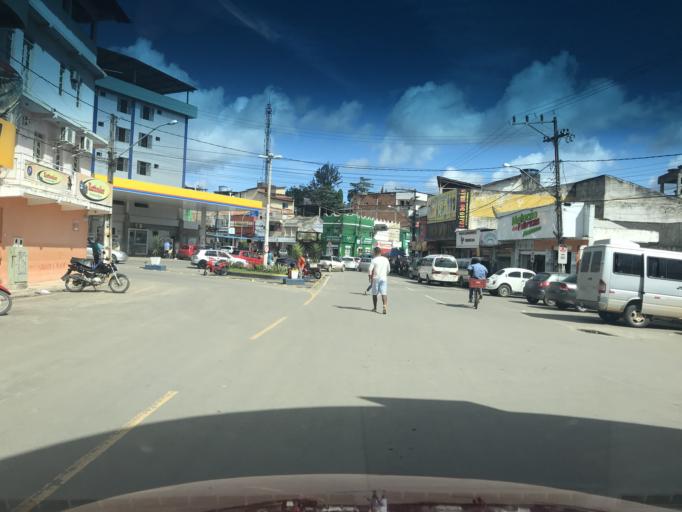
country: BR
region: Bahia
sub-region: Gandu
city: Gandu
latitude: -13.7446
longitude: -39.4860
